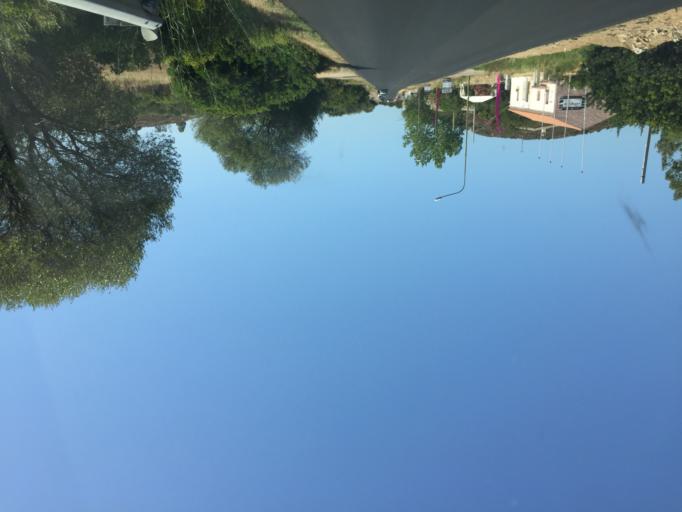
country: IT
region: Sardinia
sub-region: Provincia di Olbia-Tempio
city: San Teodoro
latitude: 40.8219
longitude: 9.6594
